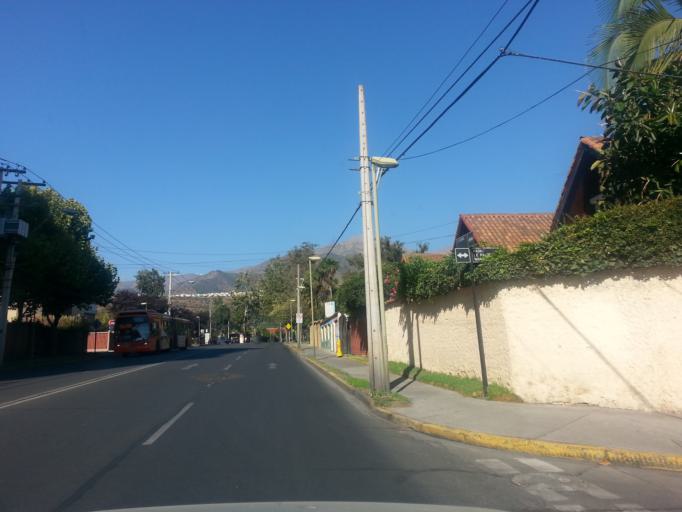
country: CL
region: Santiago Metropolitan
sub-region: Provincia de Santiago
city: Villa Presidente Frei, Nunoa, Santiago, Chile
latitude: -33.4240
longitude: -70.5398
